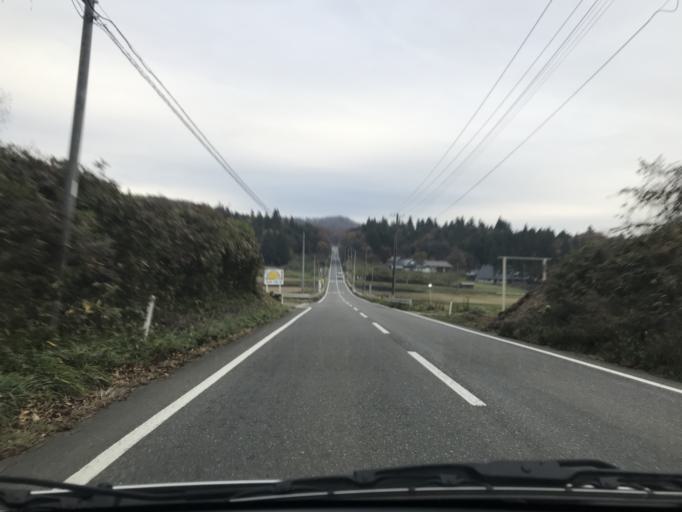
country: JP
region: Iwate
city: Kitakami
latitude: 39.2875
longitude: 141.2227
